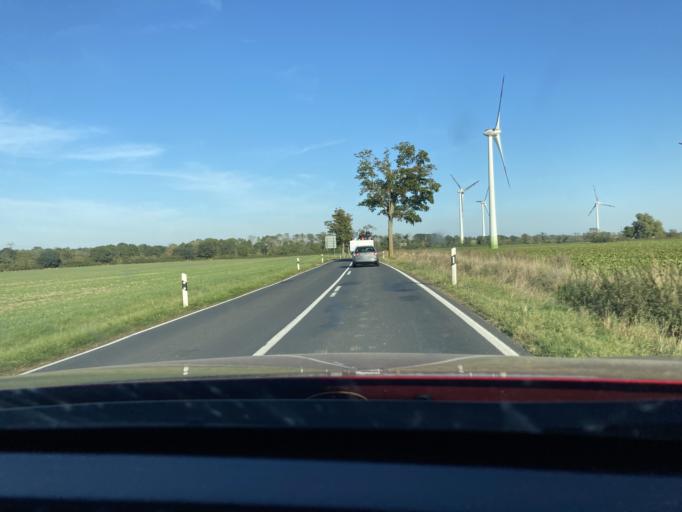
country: DE
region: Mecklenburg-Vorpommern
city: Jarmen
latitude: 53.8842
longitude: 13.4193
